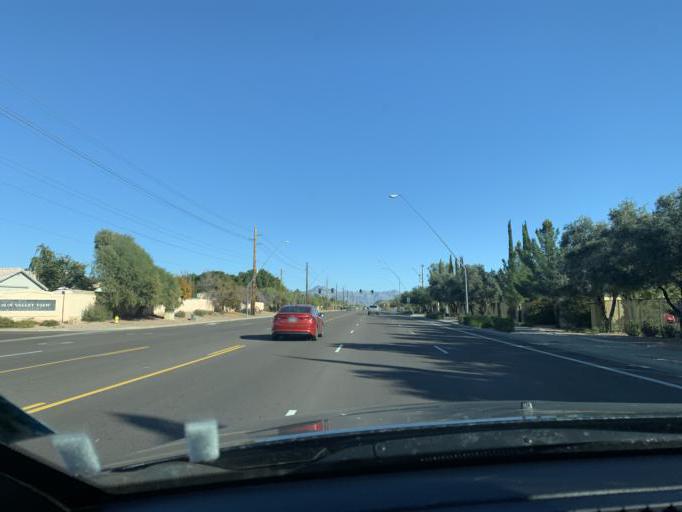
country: US
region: Arizona
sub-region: Pinal County
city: Apache Junction
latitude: 33.4224
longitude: -111.6644
